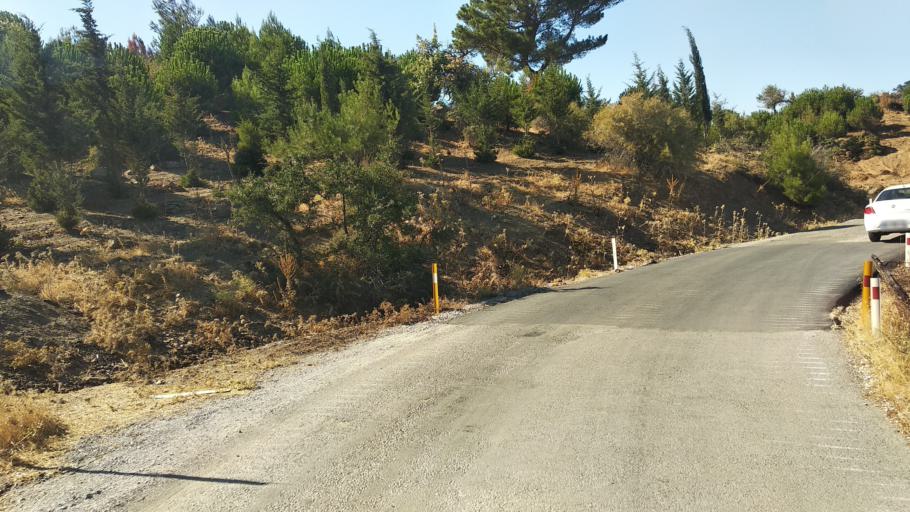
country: TR
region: Izmir
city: Gaziemir
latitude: 38.2886
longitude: 27.0018
